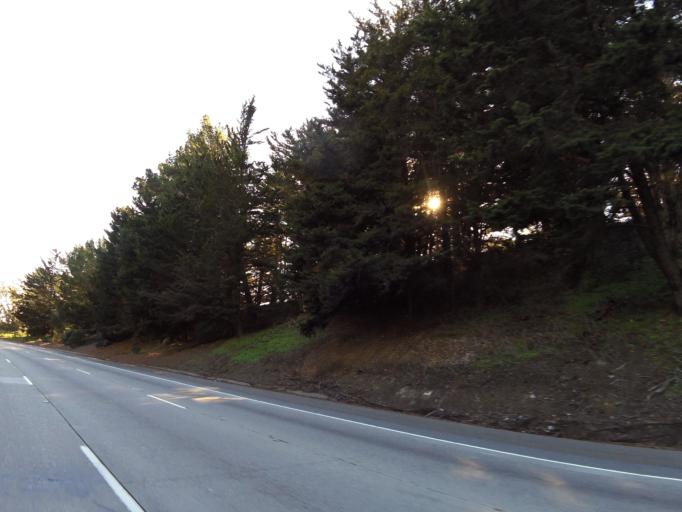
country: US
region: California
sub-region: San Mateo County
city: San Bruno
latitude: 37.6045
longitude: -122.4280
